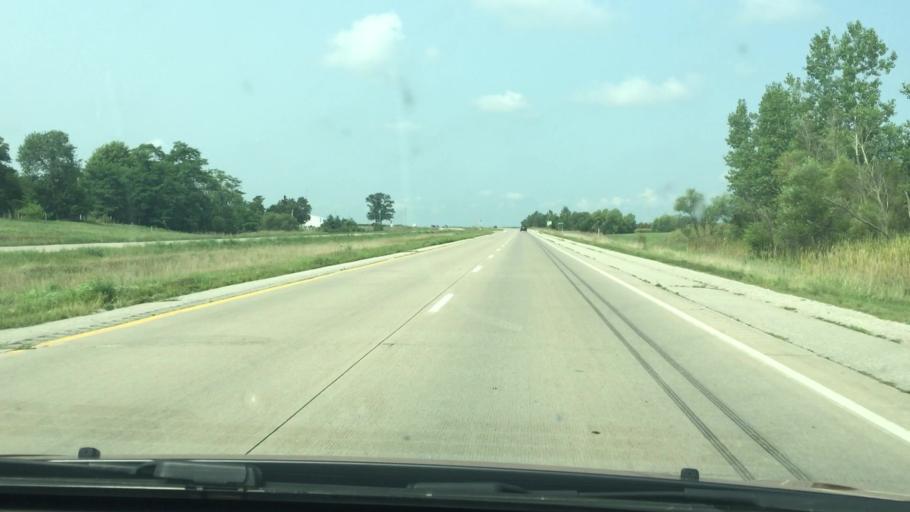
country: US
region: Iowa
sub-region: Scott County
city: Blue Grass
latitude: 41.5189
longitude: -90.8521
